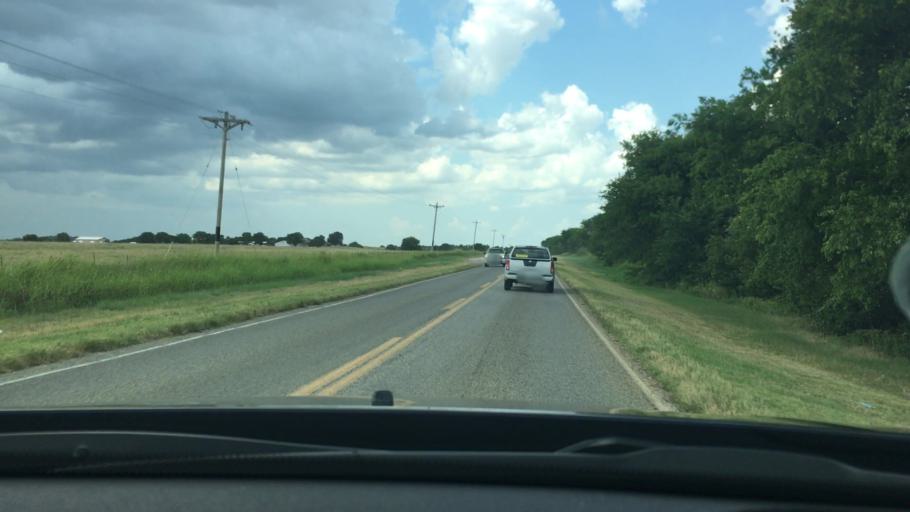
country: US
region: Oklahoma
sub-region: Pontotoc County
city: Ada
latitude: 34.5565
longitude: -96.6346
